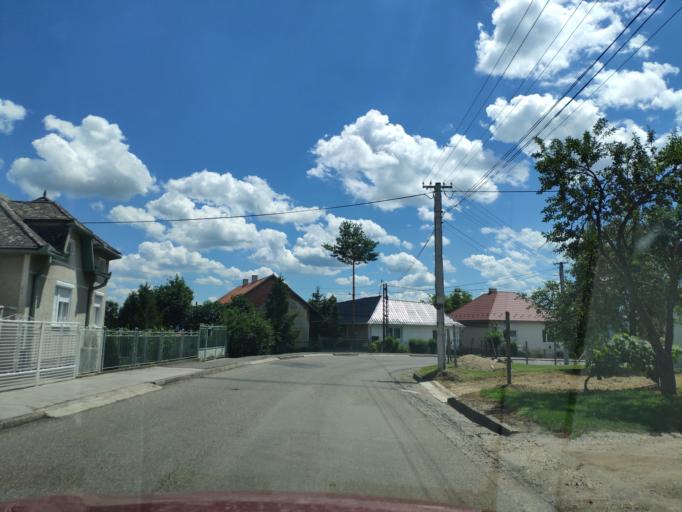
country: HU
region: Borsod-Abauj-Zemplen
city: Ozd
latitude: 48.3108
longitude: 20.2837
